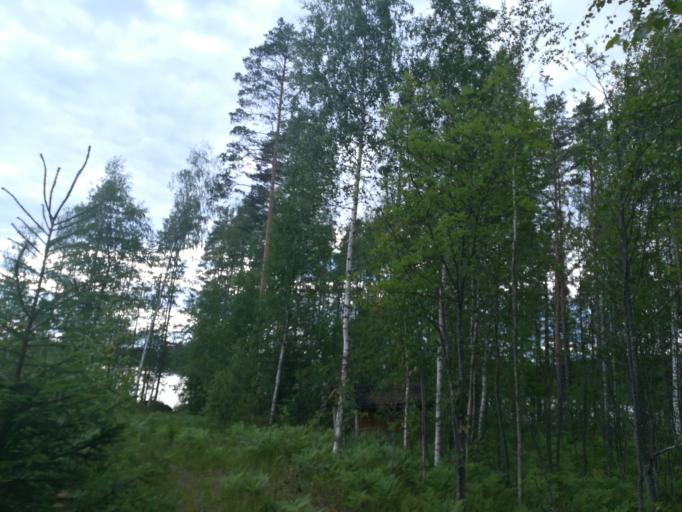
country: FI
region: South Karelia
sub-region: Lappeenranta
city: Savitaipale
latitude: 61.5029
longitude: 27.8368
